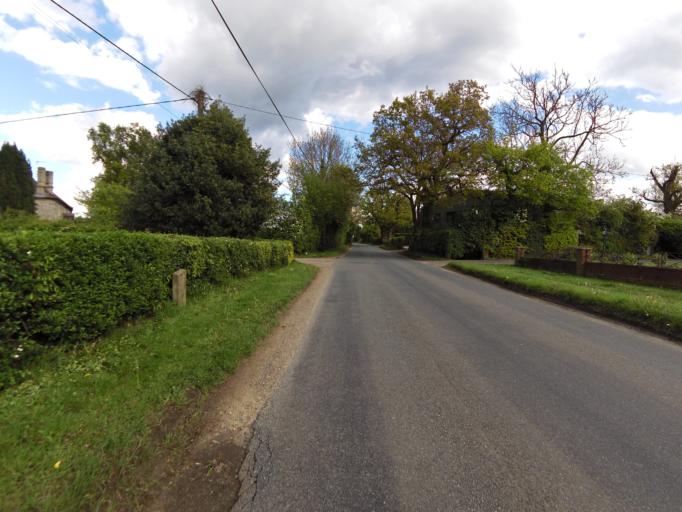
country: GB
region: England
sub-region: Suffolk
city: Elmswell
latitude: 52.2137
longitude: 0.9087
